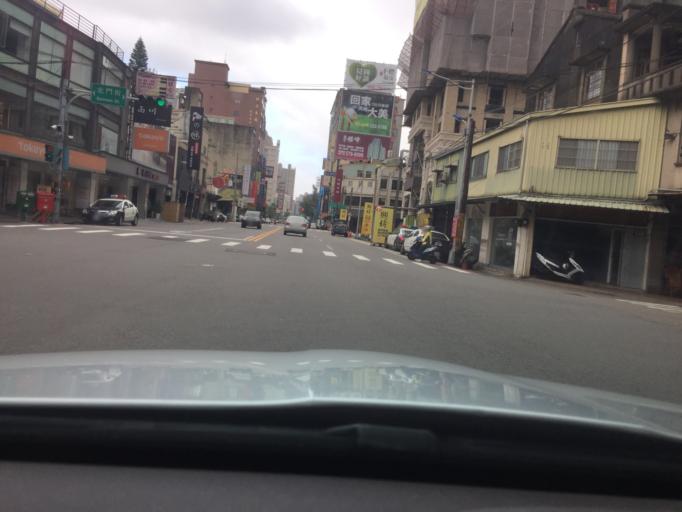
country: TW
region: Taiwan
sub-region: Hsinchu
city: Hsinchu
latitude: 24.8079
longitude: 120.9651
